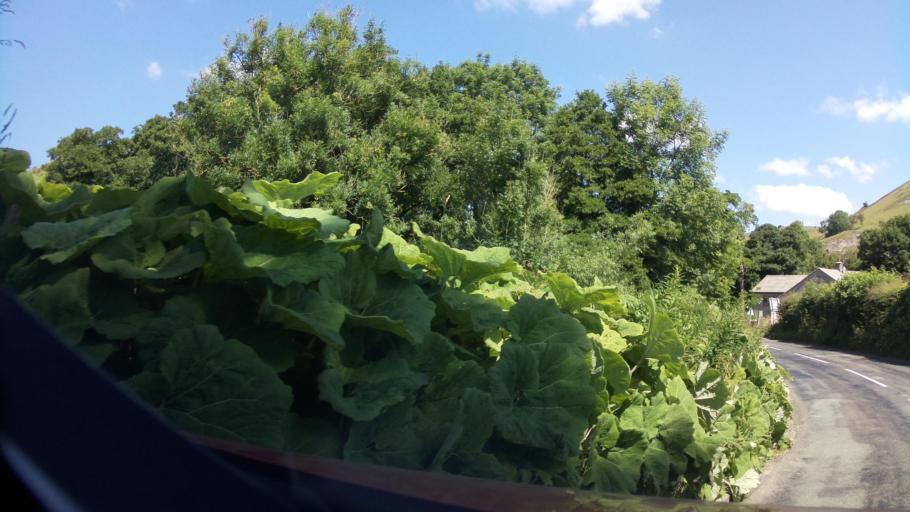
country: GB
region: England
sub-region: Derbyshire
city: Buxton
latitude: 53.1946
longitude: -1.8764
